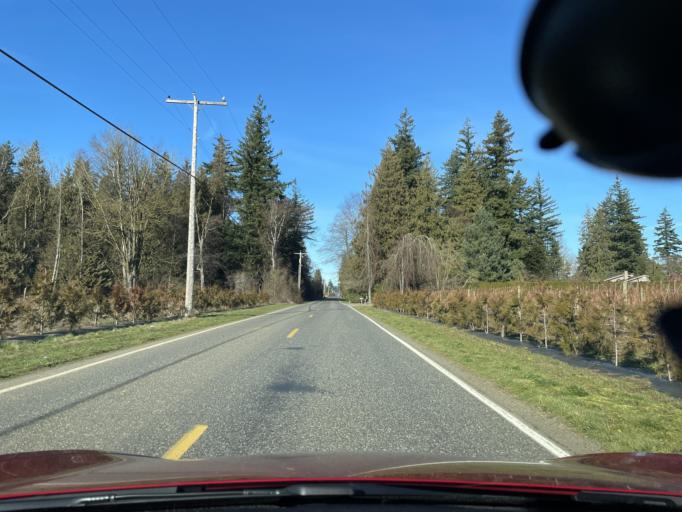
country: US
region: Washington
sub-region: Whatcom County
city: Lynden
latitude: 48.9557
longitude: -122.5303
